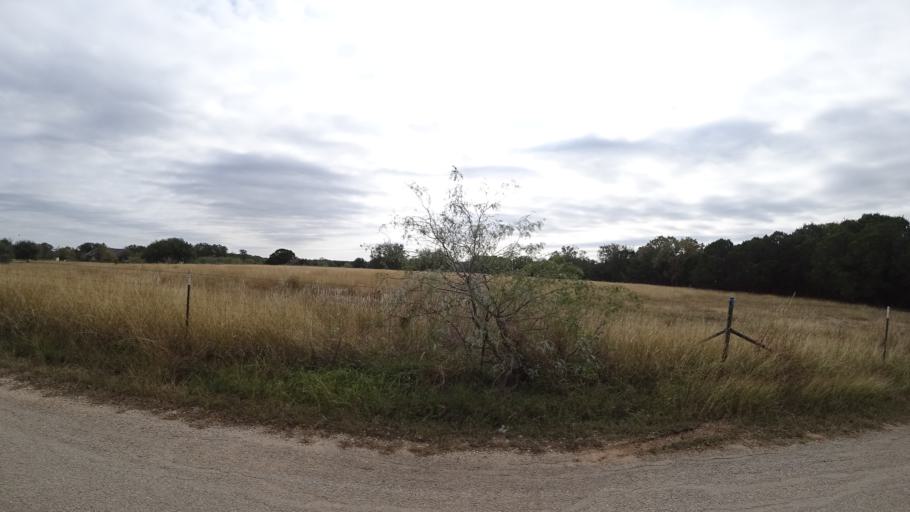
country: US
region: Texas
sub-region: Travis County
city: Shady Hollow
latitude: 30.1341
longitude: -97.8783
